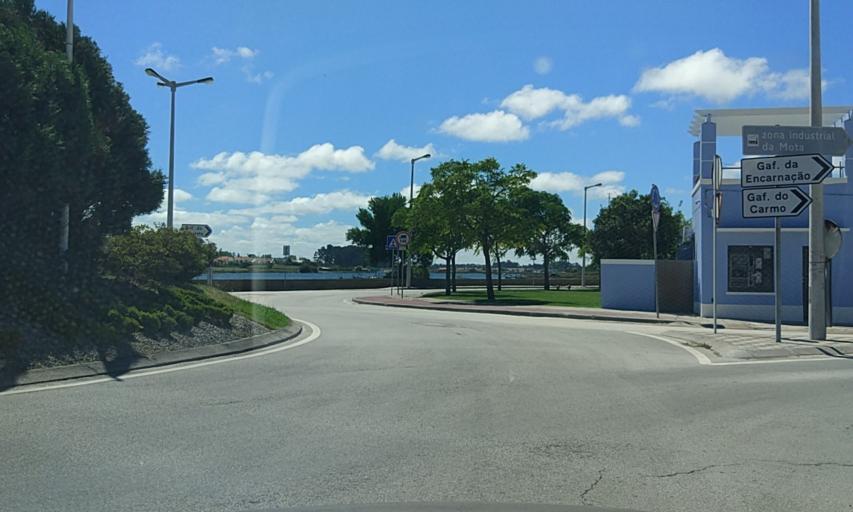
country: PT
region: Aveiro
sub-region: Ilhavo
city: Ilhavo
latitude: 40.6083
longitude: -8.6843
